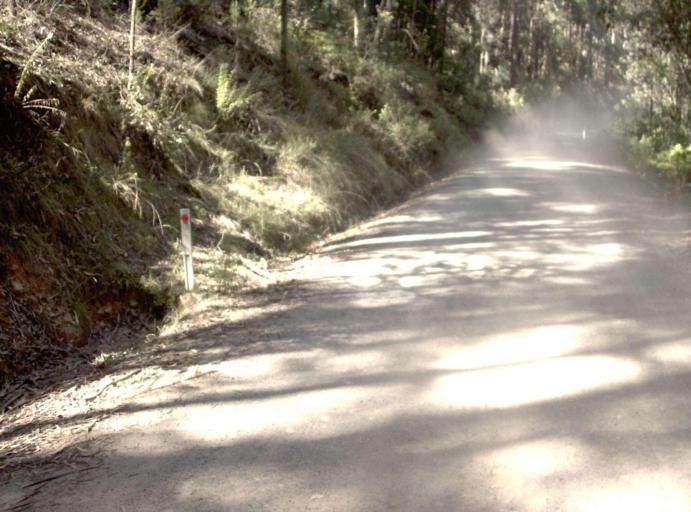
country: AU
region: New South Wales
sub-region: Bombala
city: Bombala
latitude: -37.2521
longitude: 148.7383
